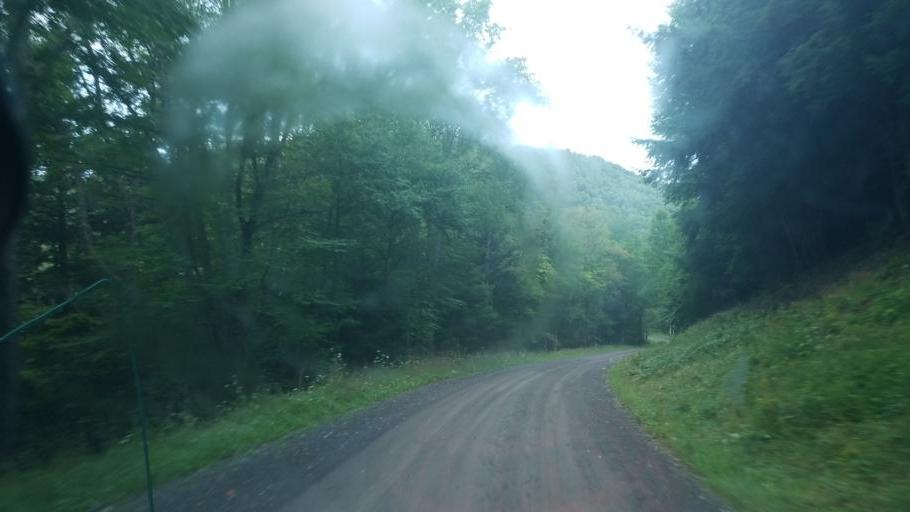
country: US
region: Pennsylvania
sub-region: Potter County
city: Galeton
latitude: 41.8408
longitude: -77.7965
